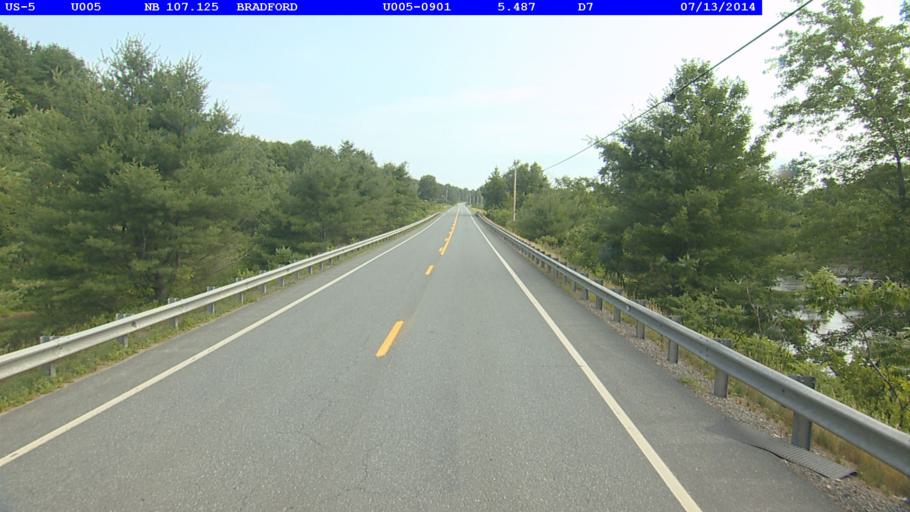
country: US
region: New Hampshire
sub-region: Grafton County
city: Haverhill
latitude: 44.0278
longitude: -72.0921
